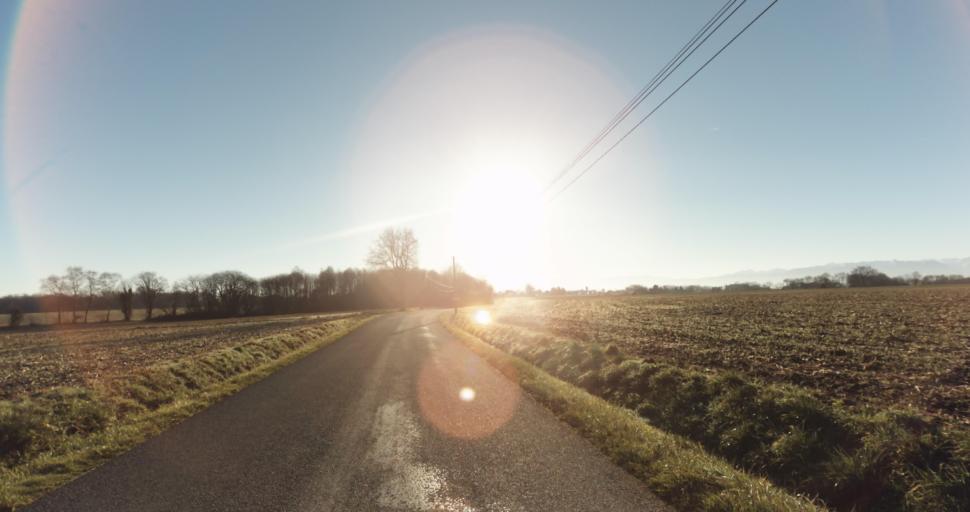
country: FR
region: Aquitaine
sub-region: Departement des Pyrenees-Atlantiques
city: Ousse
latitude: 43.3162
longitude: -0.2394
